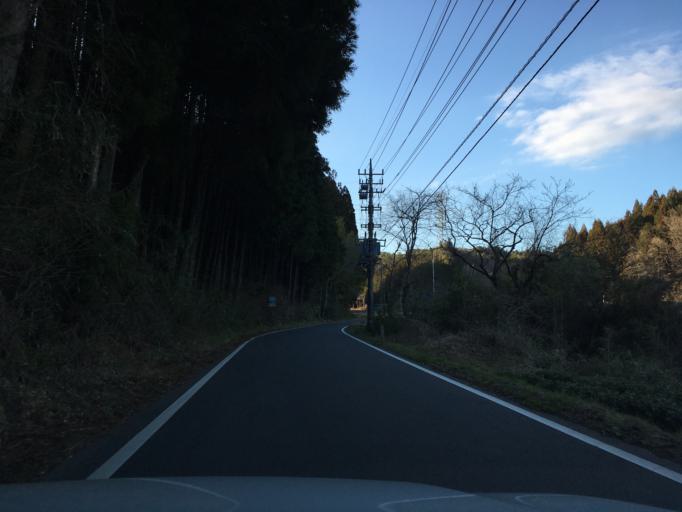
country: JP
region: Tochigi
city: Otawara
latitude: 36.8423
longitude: 140.1878
